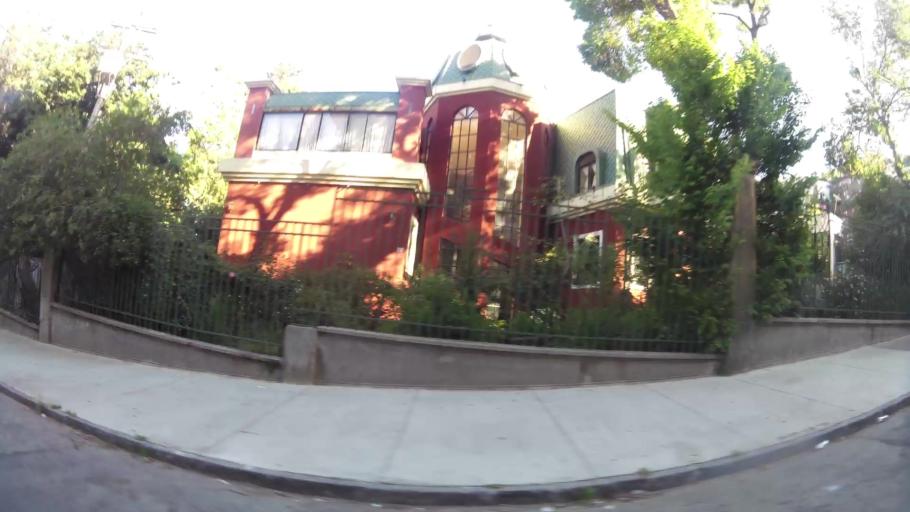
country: CL
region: Valparaiso
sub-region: Provincia de Valparaiso
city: Valparaiso
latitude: -33.0523
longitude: -71.6097
